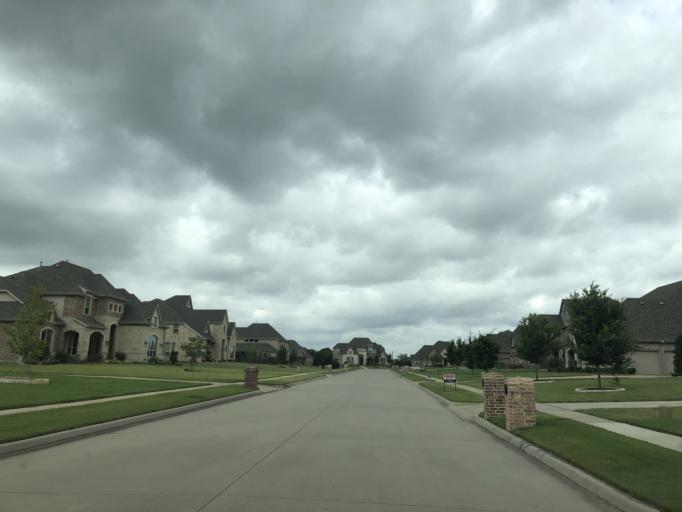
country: US
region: Texas
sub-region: Dallas County
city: Sunnyvale
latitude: 32.8131
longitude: -96.5714
